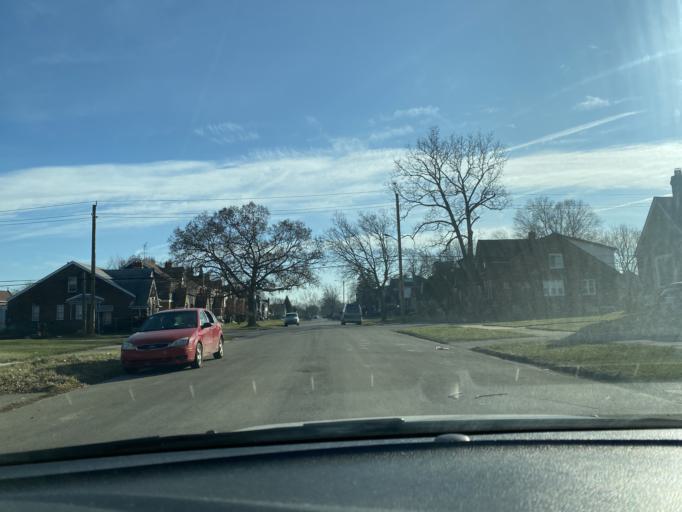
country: US
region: Michigan
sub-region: Wayne County
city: Grosse Pointe Park
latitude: 42.4068
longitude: -82.9513
